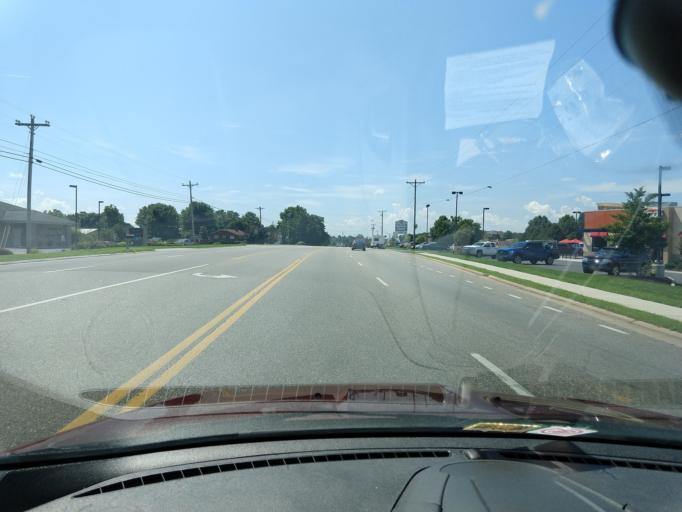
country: US
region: Virginia
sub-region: City of Harrisonburg
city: Harrisonburg
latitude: 38.4816
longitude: -78.8708
